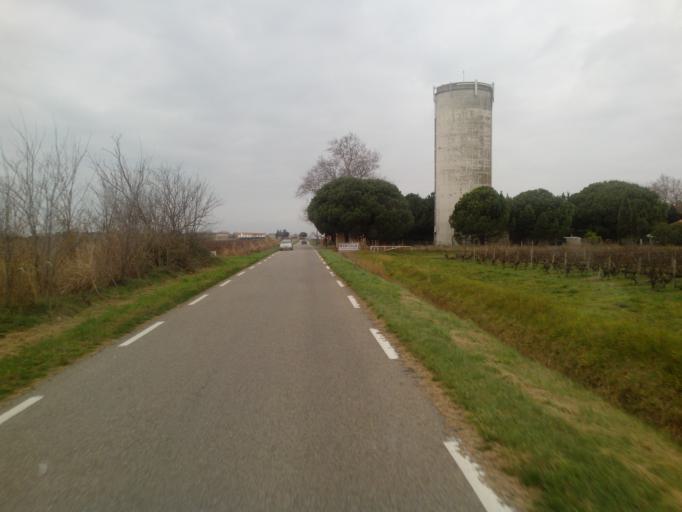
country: FR
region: Languedoc-Roussillon
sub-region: Departement du Gard
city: Aigues-Mortes
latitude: 43.5706
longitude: 4.3154
